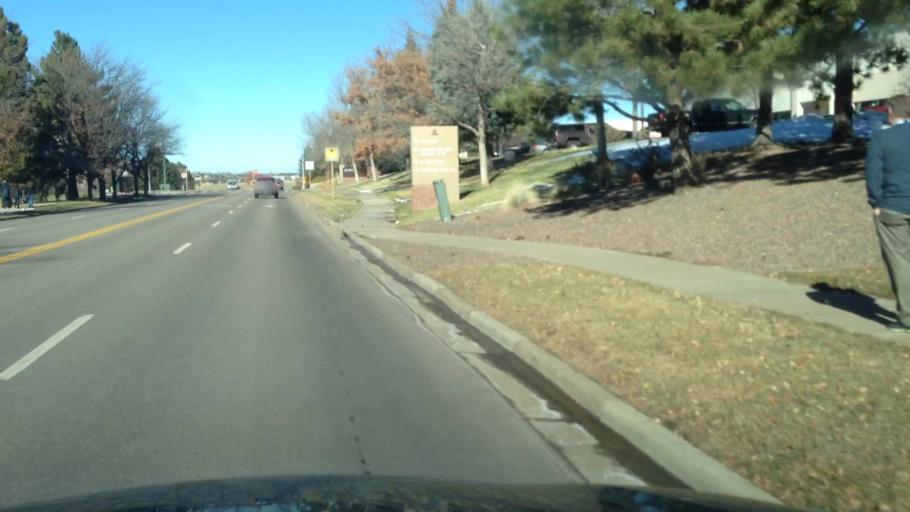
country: US
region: Colorado
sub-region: Arapahoe County
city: Centennial
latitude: 39.5791
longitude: -104.8568
